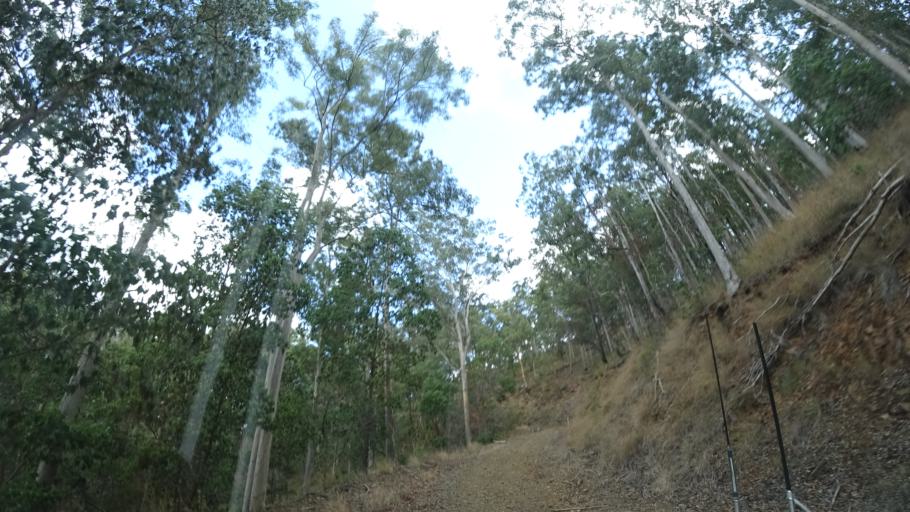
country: AU
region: Queensland
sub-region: Moreton Bay
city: Highvale
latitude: -27.3436
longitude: 152.7282
